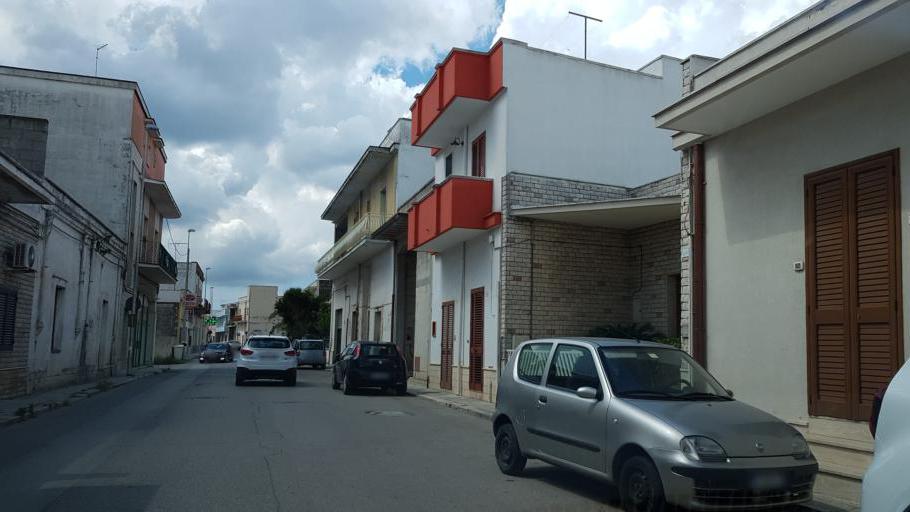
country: IT
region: Apulia
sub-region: Provincia di Brindisi
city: San Pancrazio Salentino
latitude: 40.4217
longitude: 17.8407
